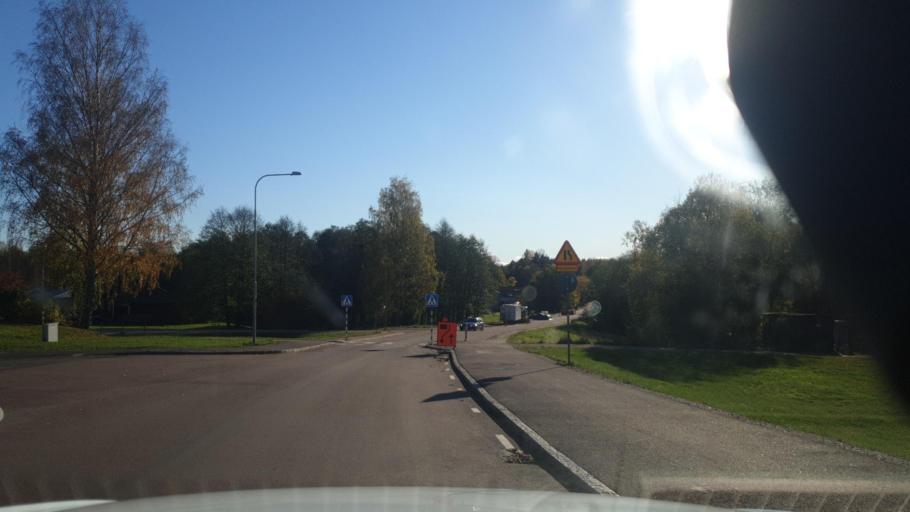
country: SE
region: Vaermland
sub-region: Arvika Kommun
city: Arvika
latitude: 59.6331
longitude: 12.8202
